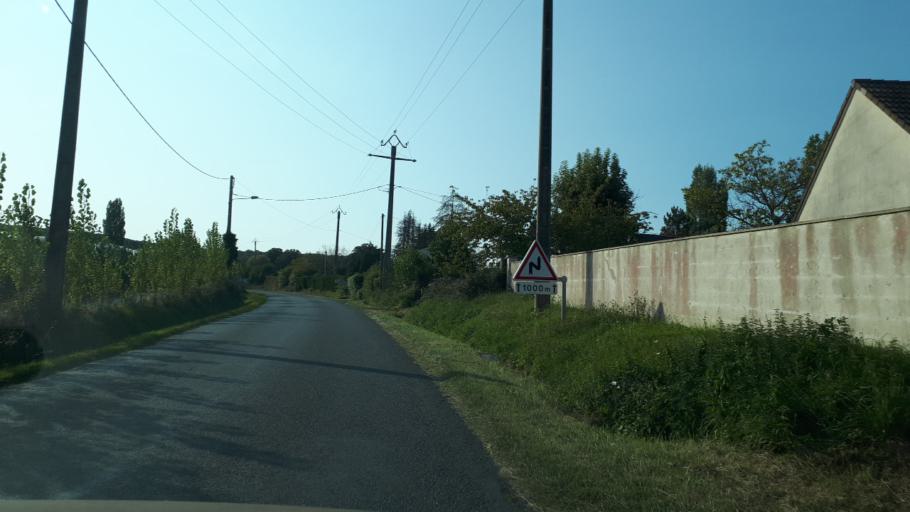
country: FR
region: Centre
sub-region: Departement du Cher
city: Vasselay
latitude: 47.2153
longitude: 2.3792
